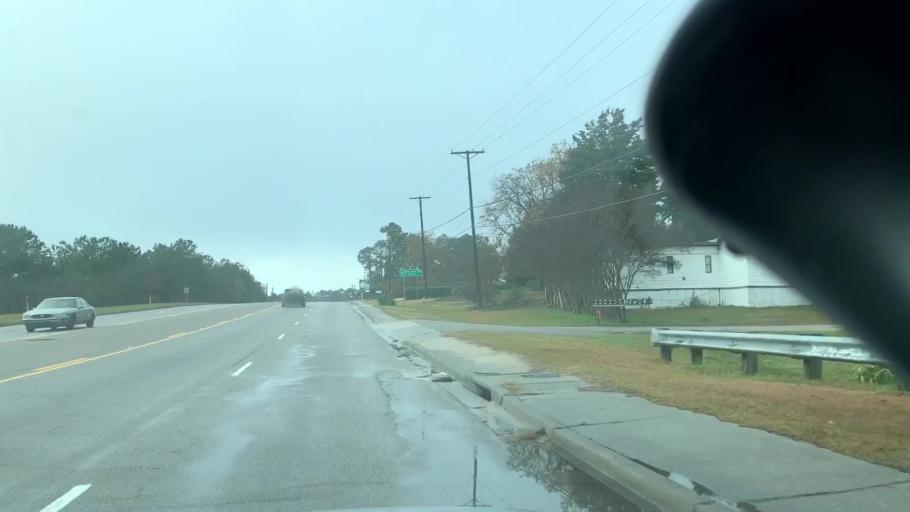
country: US
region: South Carolina
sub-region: Richland County
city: Woodfield
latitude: 34.0467
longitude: -80.9311
